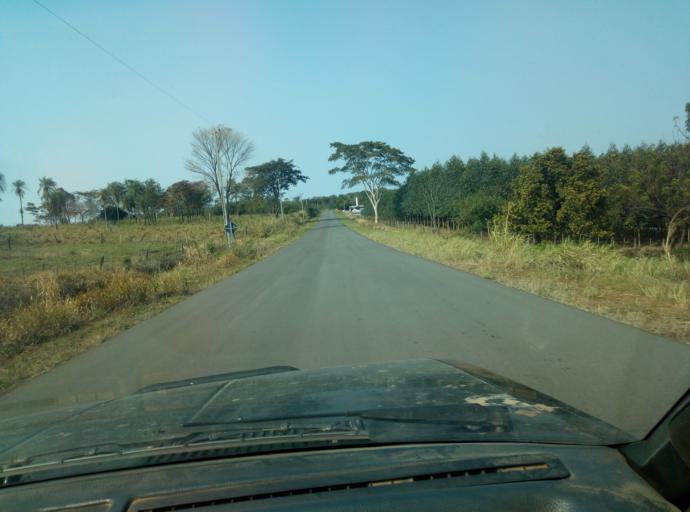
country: PY
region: Caaguazu
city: Carayao
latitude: -25.1986
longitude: -56.3085
